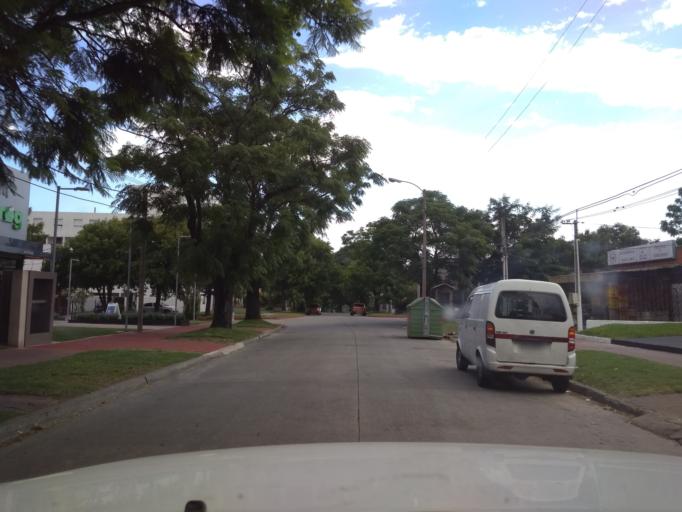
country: UY
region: Canelones
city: Paso de Carrasco
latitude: -34.8884
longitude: -56.0844
